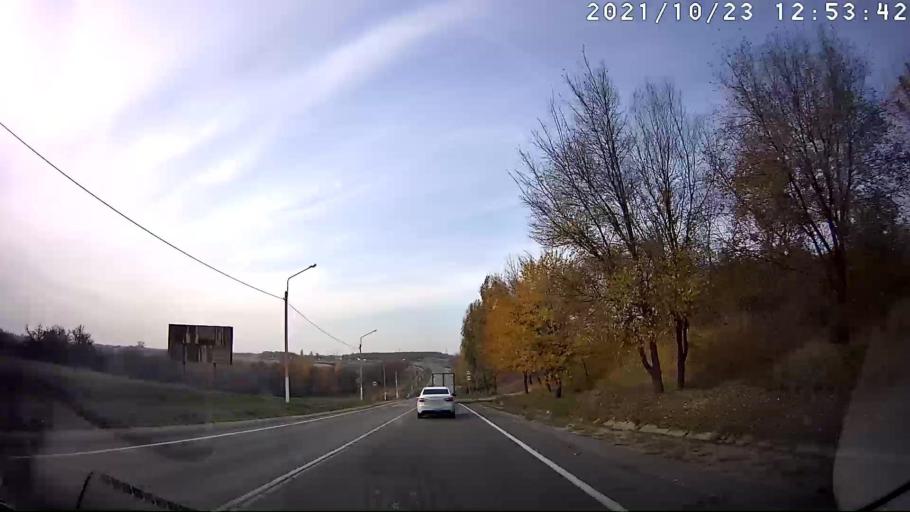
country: RU
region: Volgograd
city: Dubovka
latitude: 49.0572
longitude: 44.8103
